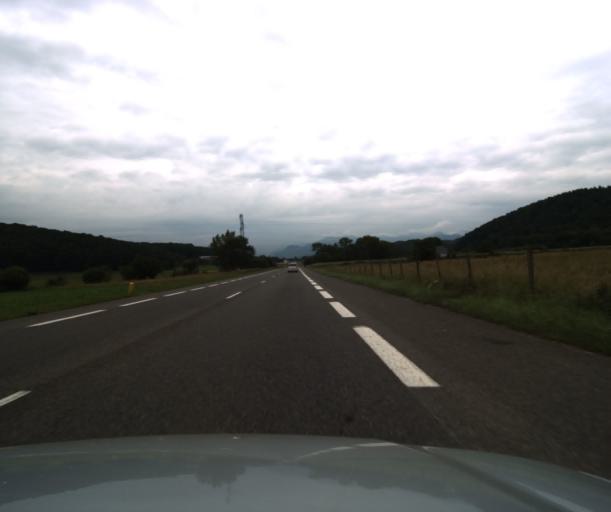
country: FR
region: Midi-Pyrenees
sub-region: Departement des Hautes-Pyrenees
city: Ossun
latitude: 43.1517
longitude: -0.0223
